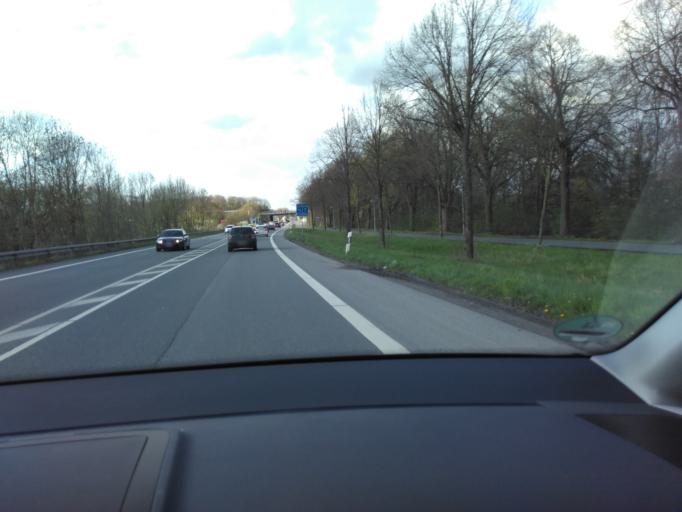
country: DE
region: North Rhine-Westphalia
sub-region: Regierungsbezirk Munster
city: Beckum
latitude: 51.7758
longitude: 8.0341
